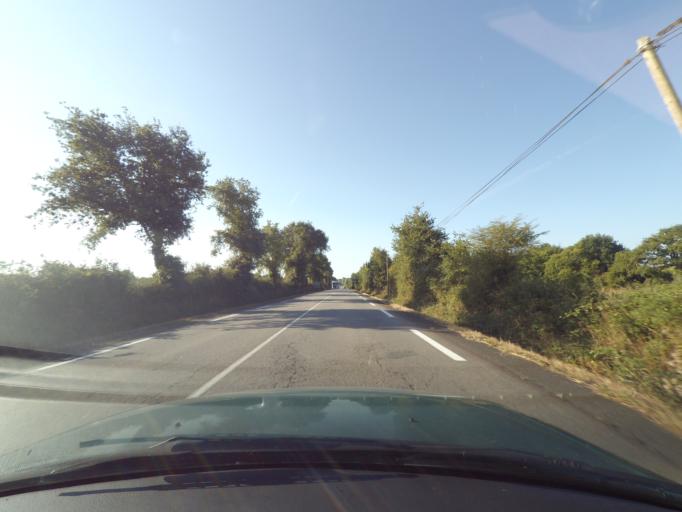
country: FR
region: Poitou-Charentes
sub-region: Departement des Deux-Sevres
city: Chiche
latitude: 46.7510
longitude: -0.3075
